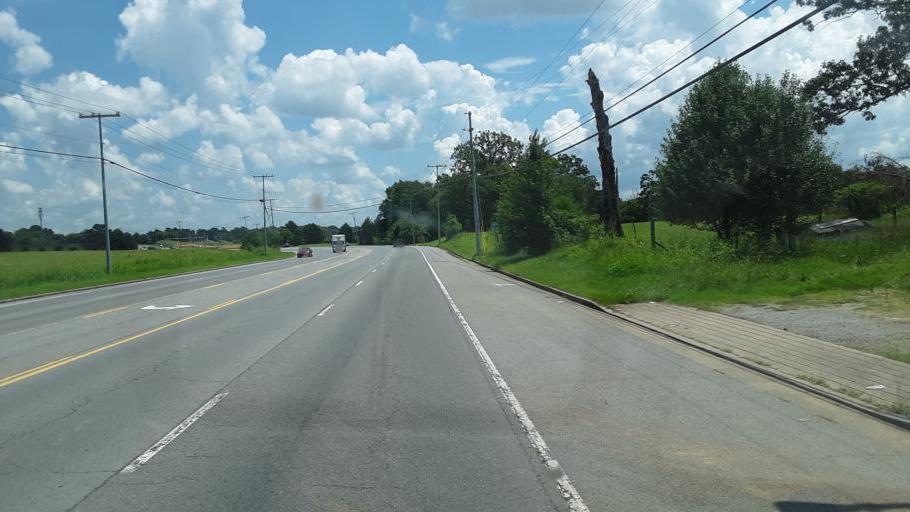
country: US
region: Kentucky
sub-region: Christian County
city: Oak Grove
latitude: 36.6303
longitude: -87.3927
